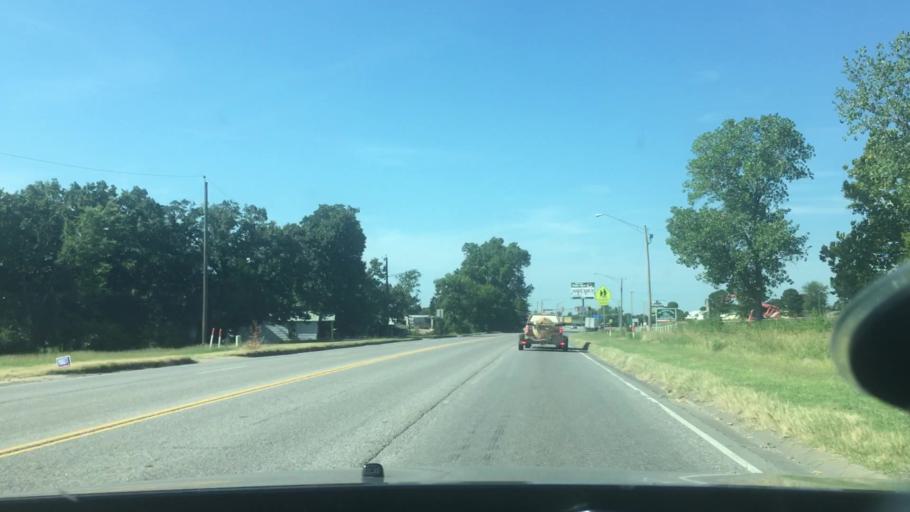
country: US
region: Oklahoma
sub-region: Atoka County
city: Atoka
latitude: 34.3193
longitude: -96.1677
